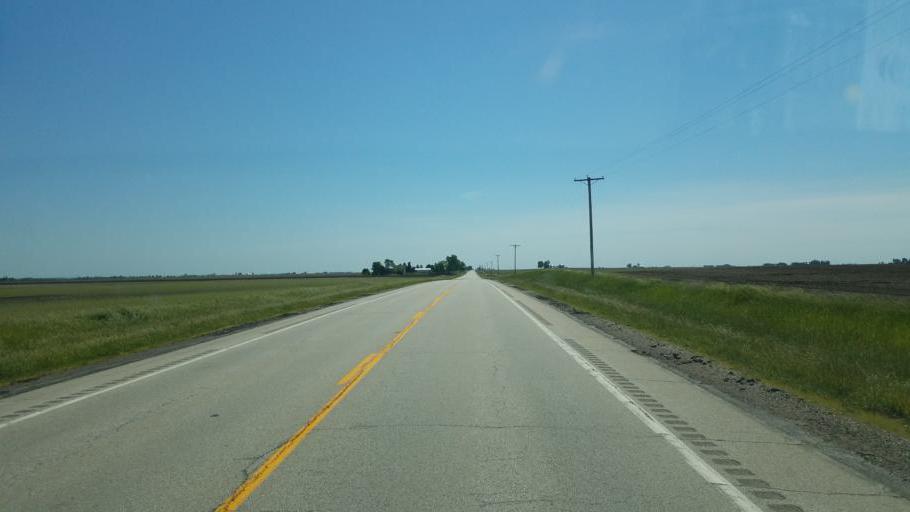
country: US
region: Illinois
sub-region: McLean County
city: Heyworth
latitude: 40.3123
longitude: -88.9112
